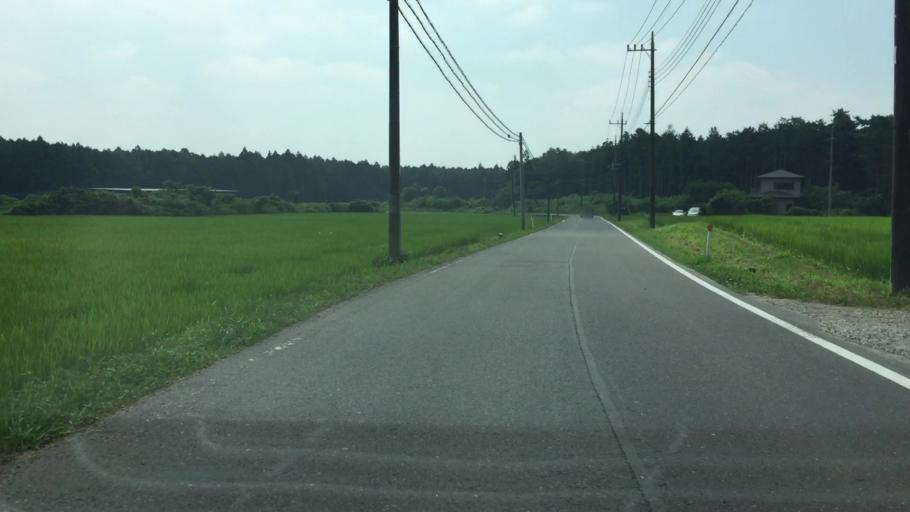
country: JP
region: Tochigi
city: Kuroiso
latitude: 36.9575
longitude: 139.9560
